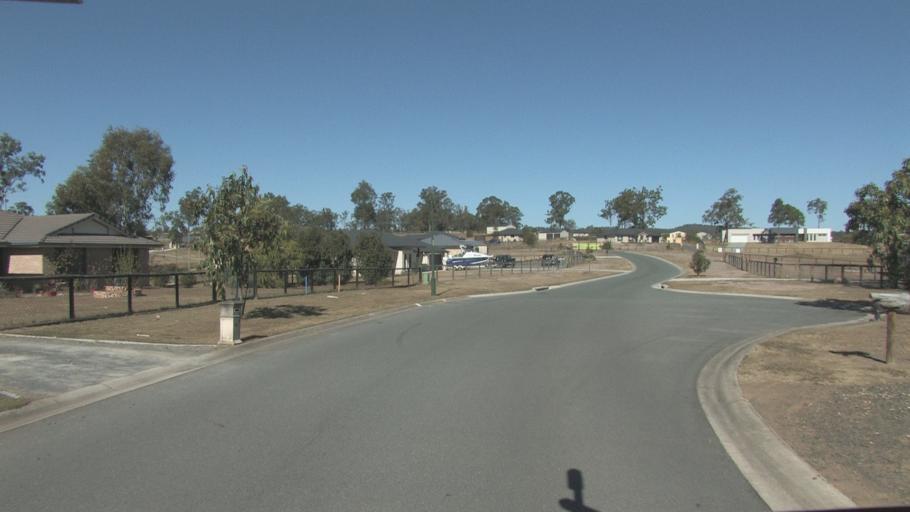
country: AU
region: Queensland
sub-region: Logan
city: Cedar Vale
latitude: -27.8608
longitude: 153.0466
